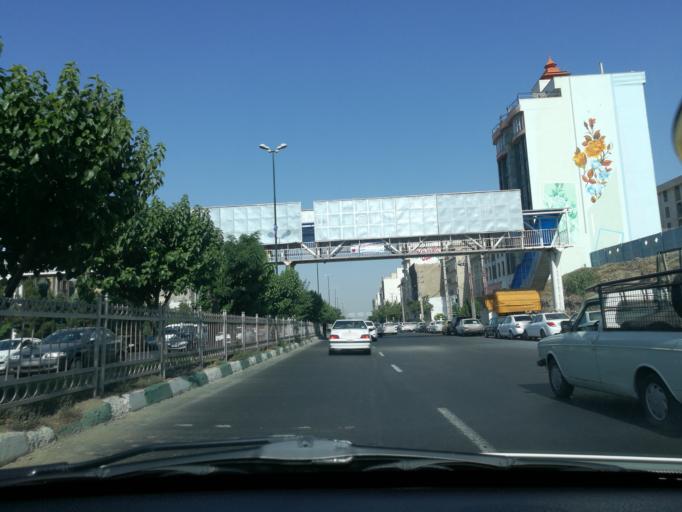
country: IR
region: Alborz
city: Karaj
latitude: 35.8309
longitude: 51.0077
